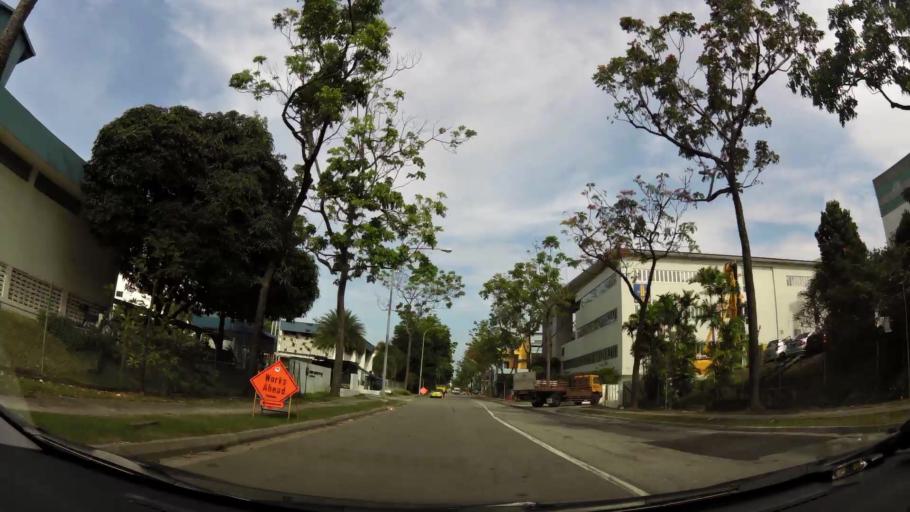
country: MY
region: Johor
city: Johor Bahru
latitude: 1.3231
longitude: 103.6439
